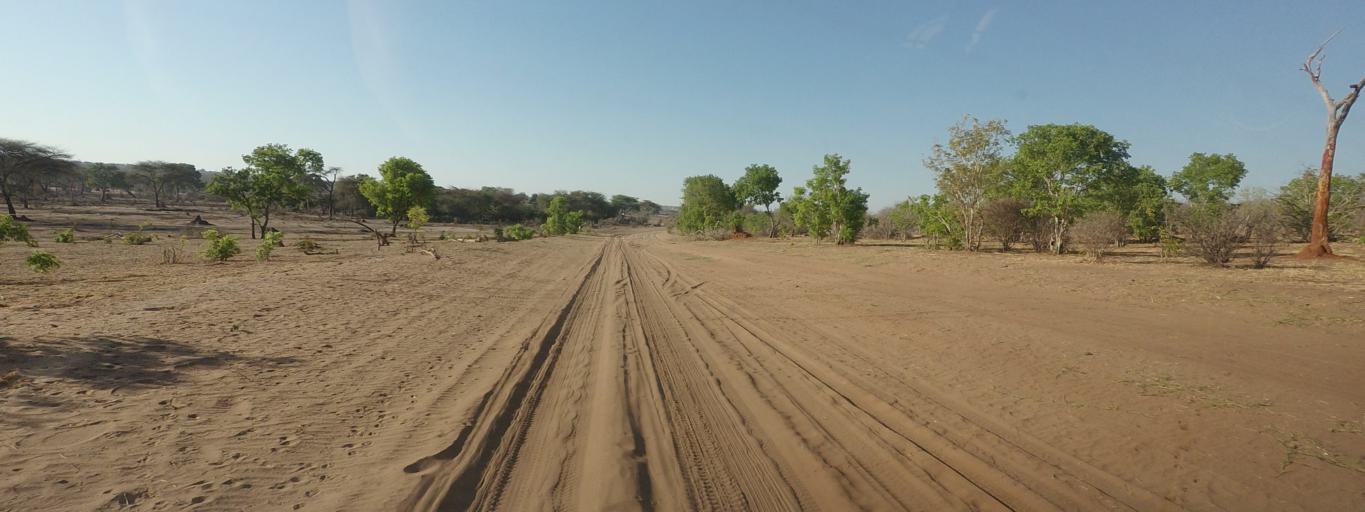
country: BW
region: North West
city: Kasane
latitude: -17.8777
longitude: 25.2344
